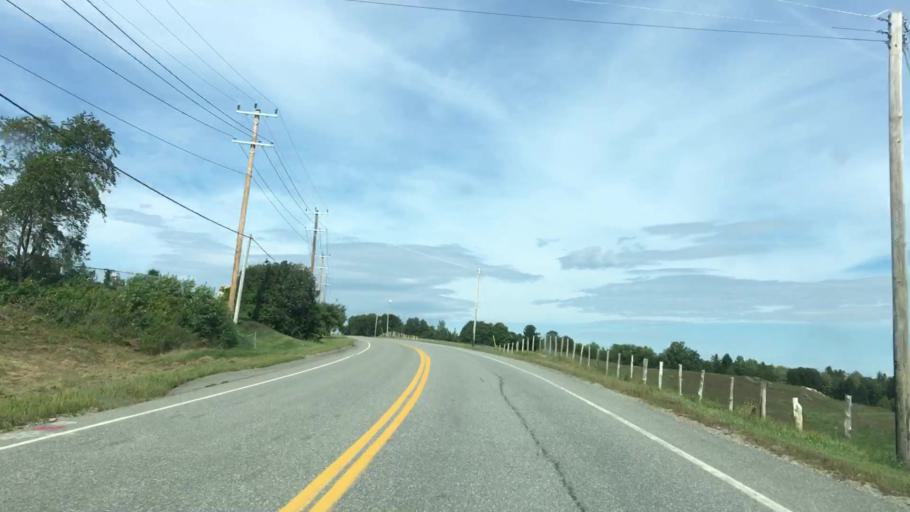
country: US
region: Maine
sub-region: Penobscot County
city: Lincoln
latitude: 45.3970
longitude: -68.5111
